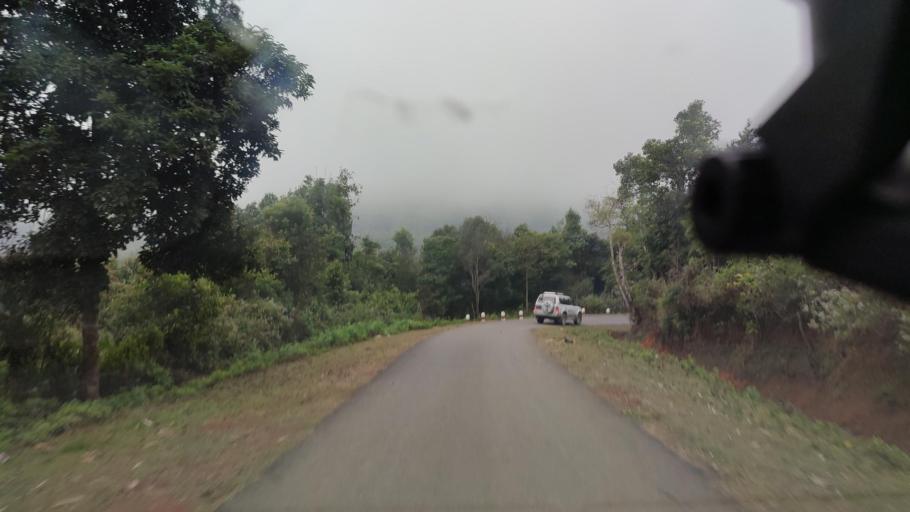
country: TH
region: Chiang Rai
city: Mae Sai
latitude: 21.1134
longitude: 99.6171
